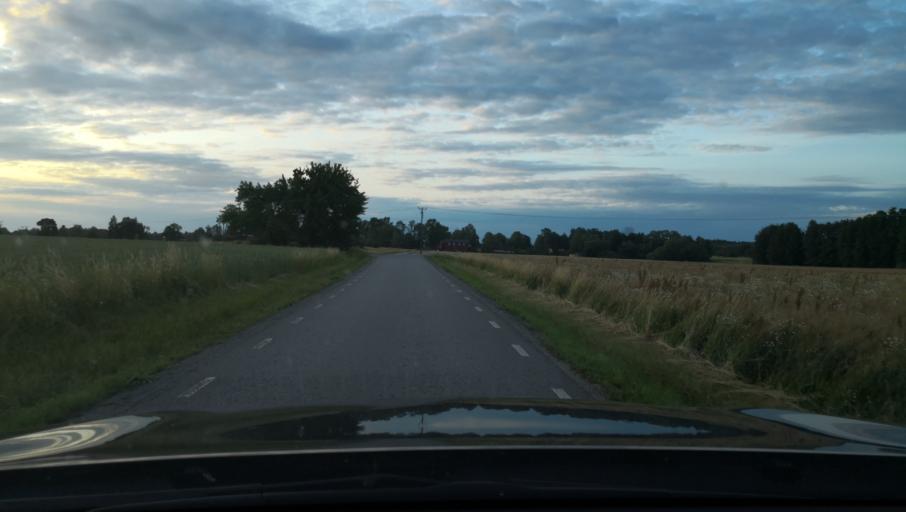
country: SE
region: Uppsala
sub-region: Uppsala Kommun
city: Vattholma
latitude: 60.0330
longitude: 17.6648
